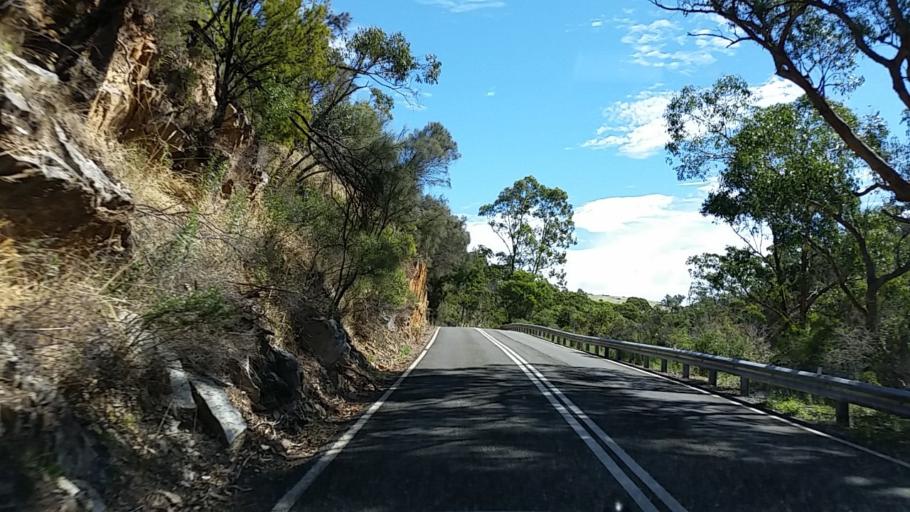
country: AU
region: South Australia
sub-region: Adelaide Hills
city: Gumeracha
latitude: -34.8415
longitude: 138.8420
